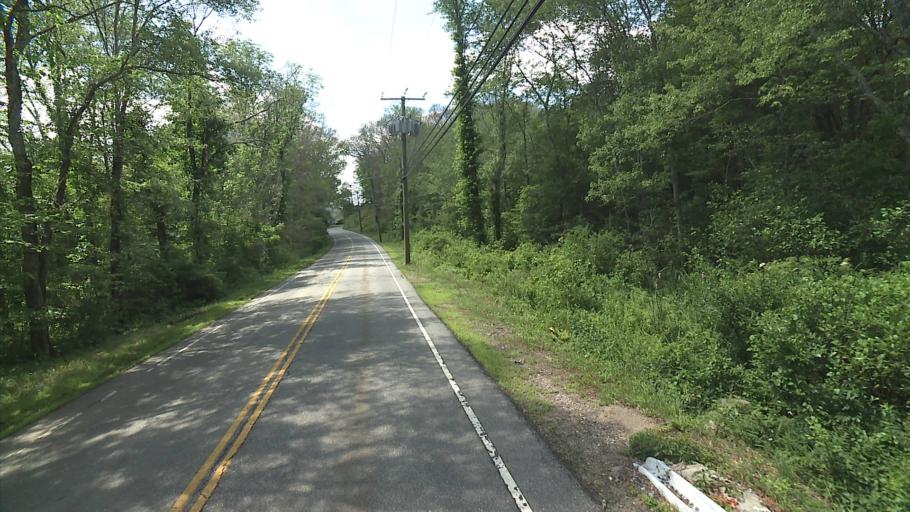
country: US
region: Connecticut
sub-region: Middlesex County
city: Moodus
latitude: 41.5026
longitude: -72.4719
